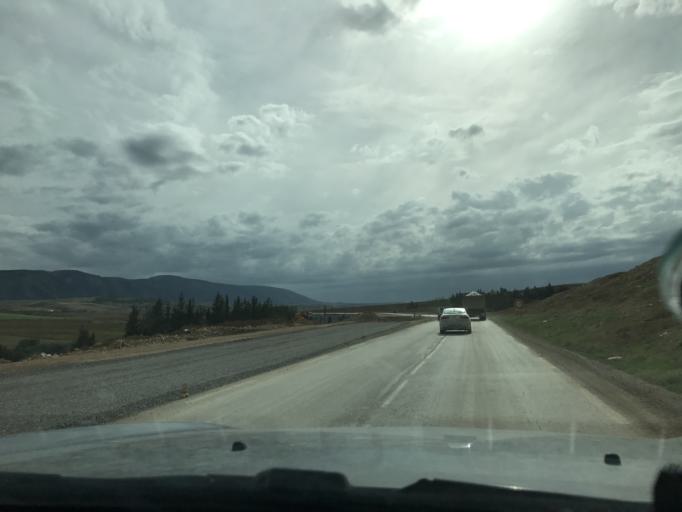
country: TN
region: Silyanah
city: Bu `Aradah
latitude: 36.1517
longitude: 9.6341
